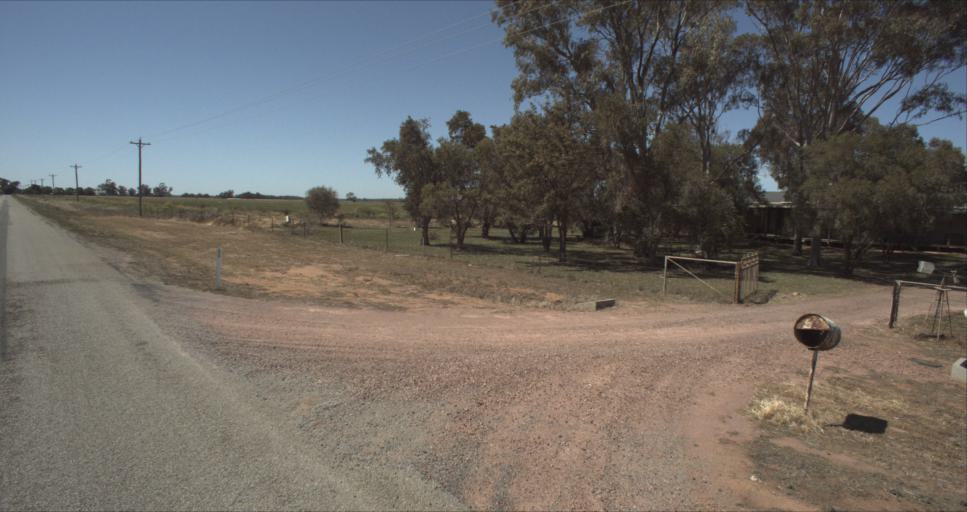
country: AU
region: New South Wales
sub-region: Leeton
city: Leeton
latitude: -34.5824
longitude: 146.3009
